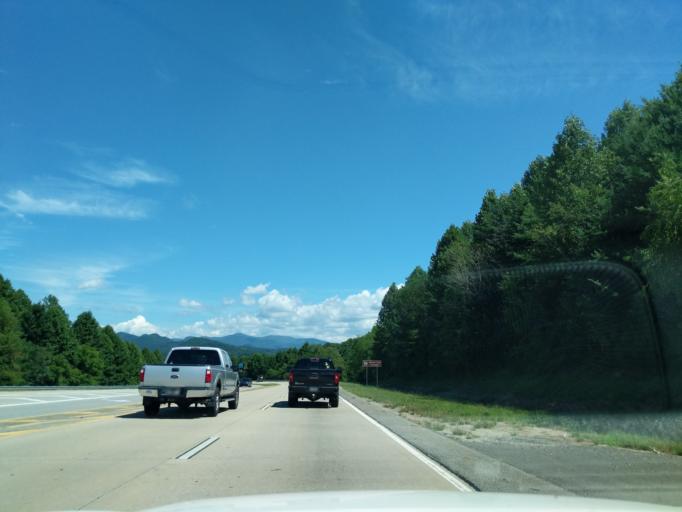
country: US
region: Georgia
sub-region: Union County
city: Blairsville
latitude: 34.8606
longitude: -84.0040
